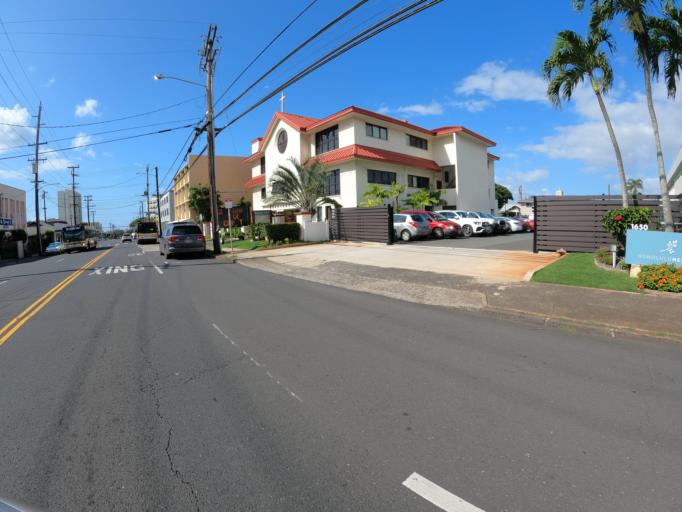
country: US
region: Hawaii
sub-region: Honolulu County
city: Honolulu
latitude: 21.3226
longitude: -157.8588
